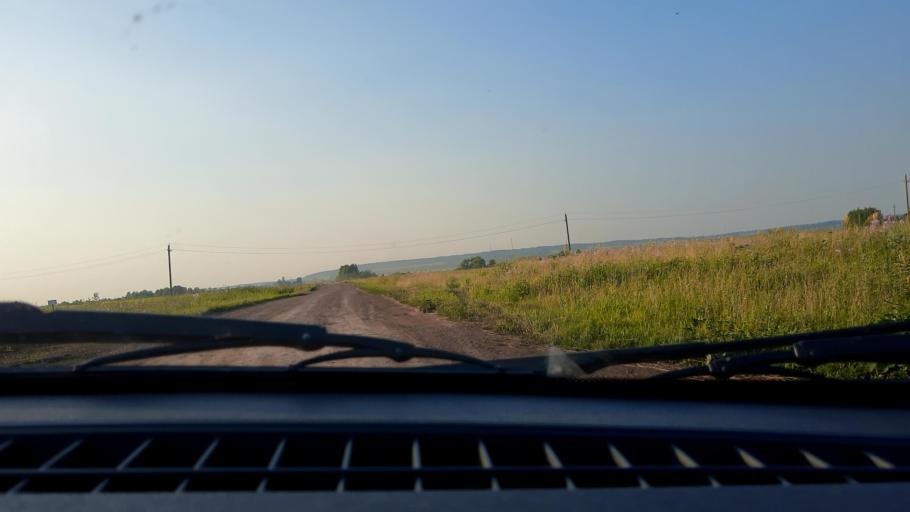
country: RU
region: Bashkortostan
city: Asanovo
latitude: 54.9342
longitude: 55.6238
